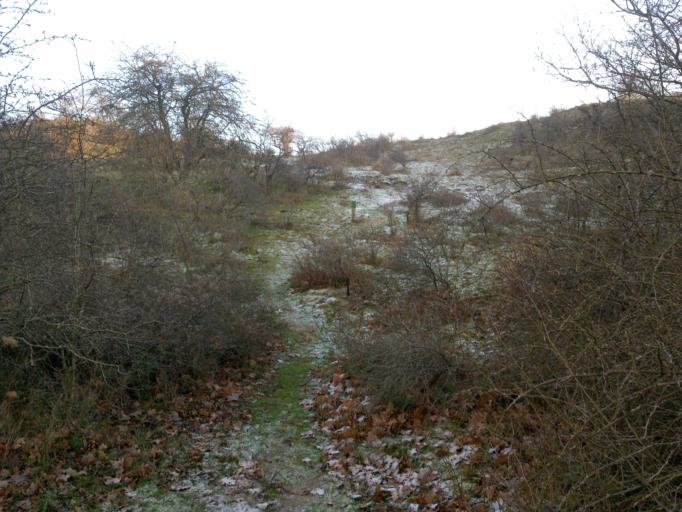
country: NL
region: South Holland
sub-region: Gemeente Wassenaar
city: Wassenaar
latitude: 52.1381
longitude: 4.3403
